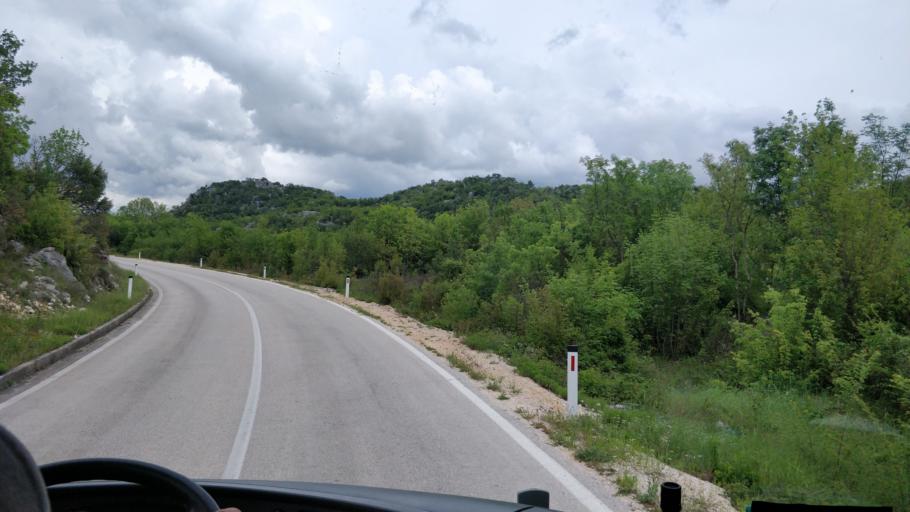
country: BA
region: Federation of Bosnia and Herzegovina
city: Ljubuski
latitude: 43.1741
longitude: 17.4898
